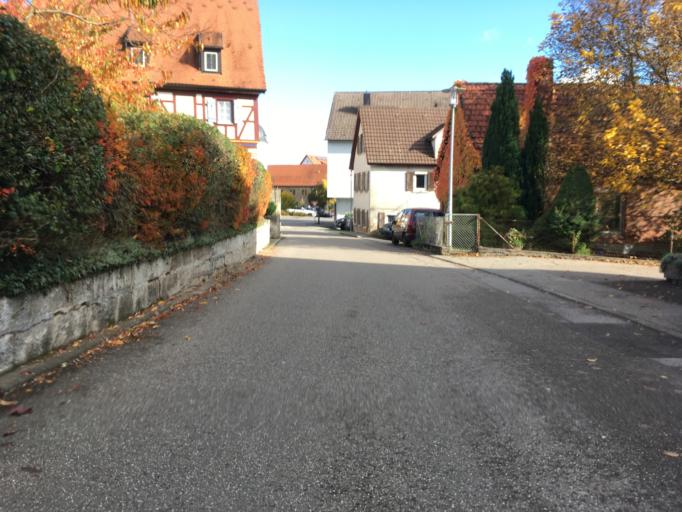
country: DE
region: Baden-Wuerttemberg
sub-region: Regierungsbezirk Stuttgart
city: Pfedelbach
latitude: 49.1758
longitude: 9.5034
